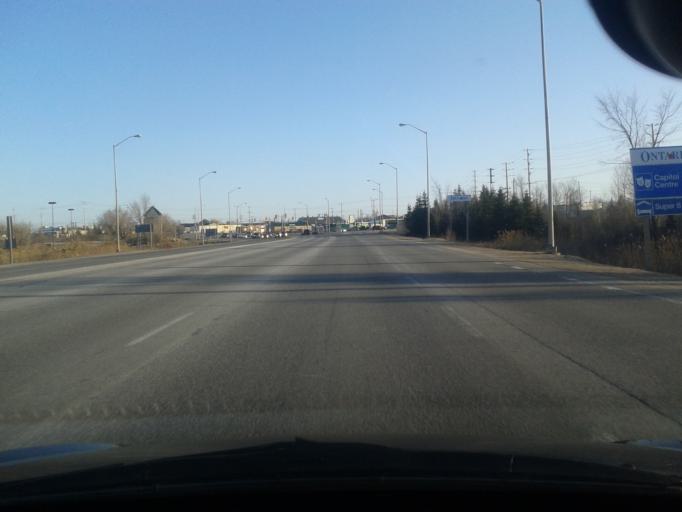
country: CA
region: Ontario
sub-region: Nipissing District
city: North Bay
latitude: 46.3149
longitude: -79.4436
